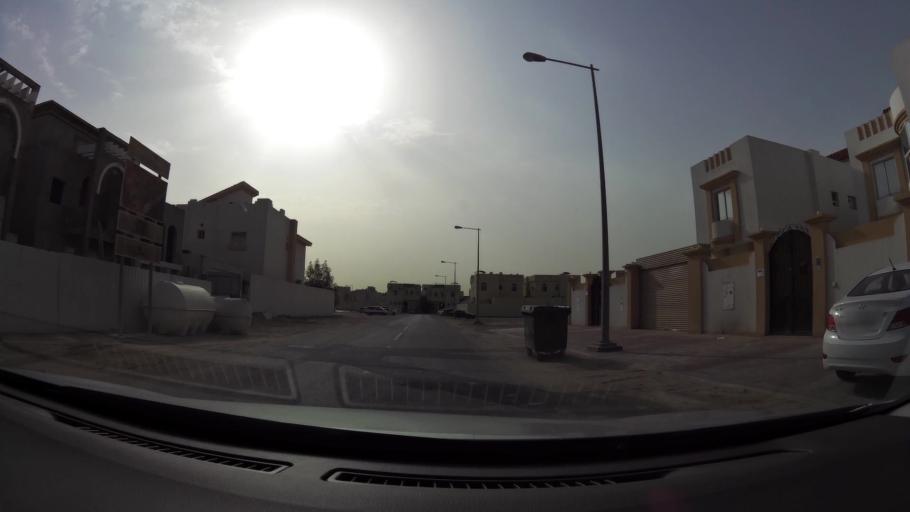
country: QA
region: Baladiyat ad Dawhah
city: Doha
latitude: 25.3206
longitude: 51.5029
